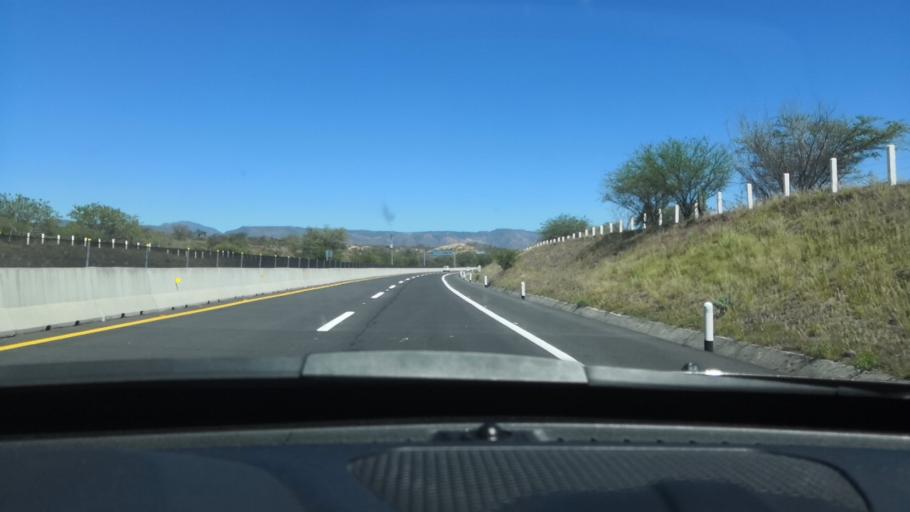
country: MX
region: Nayarit
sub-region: Ahuacatlan
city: Ahuacatlan
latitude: 21.0644
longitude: -104.5011
